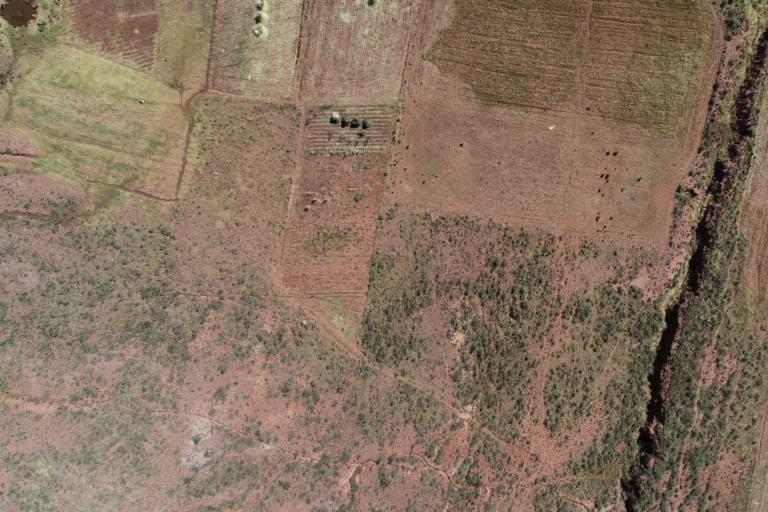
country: BO
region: La Paz
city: Tiahuanaco
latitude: -16.5952
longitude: -68.7571
